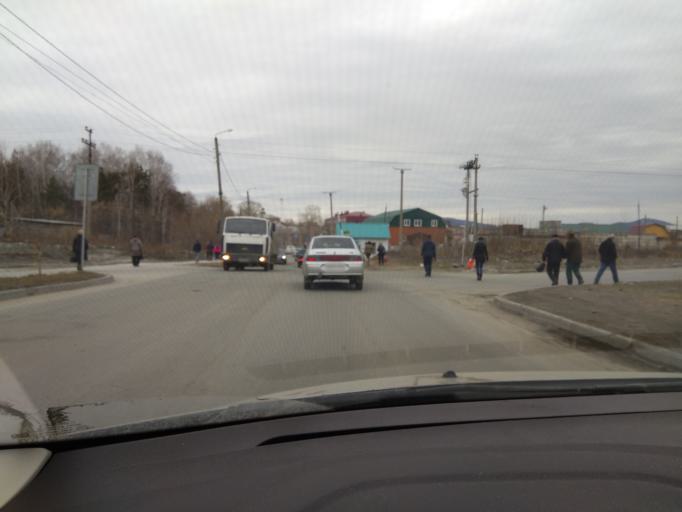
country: RU
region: Chelyabinsk
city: Kyshtym
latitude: 55.7072
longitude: 60.5670
